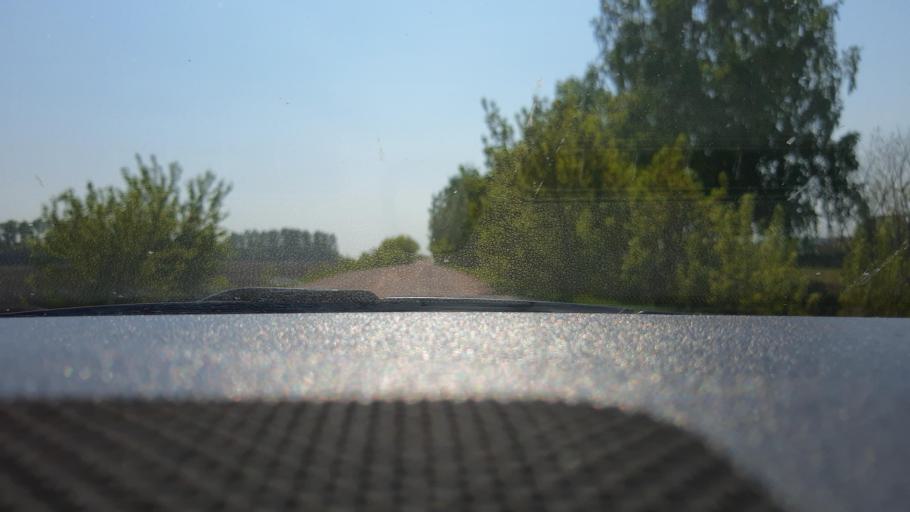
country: RU
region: Bashkortostan
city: Chishmy
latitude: 54.4388
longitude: 55.3070
